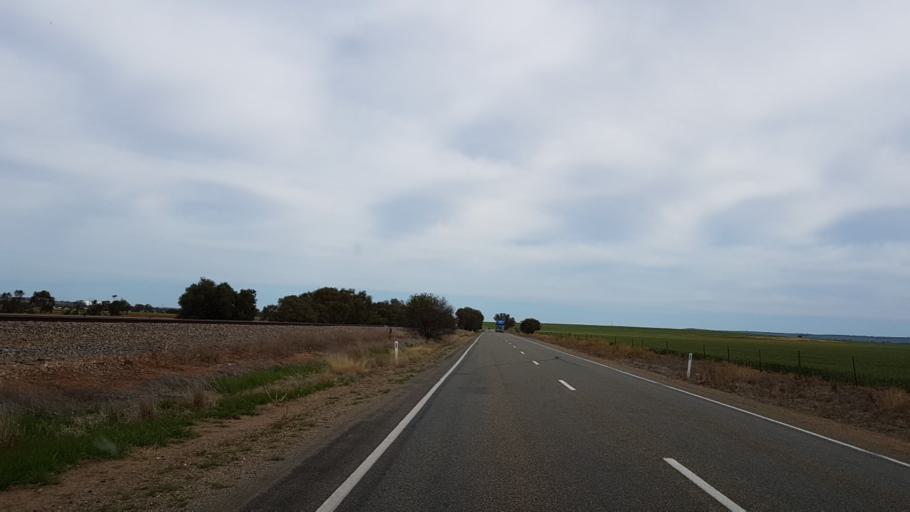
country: AU
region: South Australia
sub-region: Port Pirie City and Dists
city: Crystal Brook
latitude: -33.2455
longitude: 138.3717
